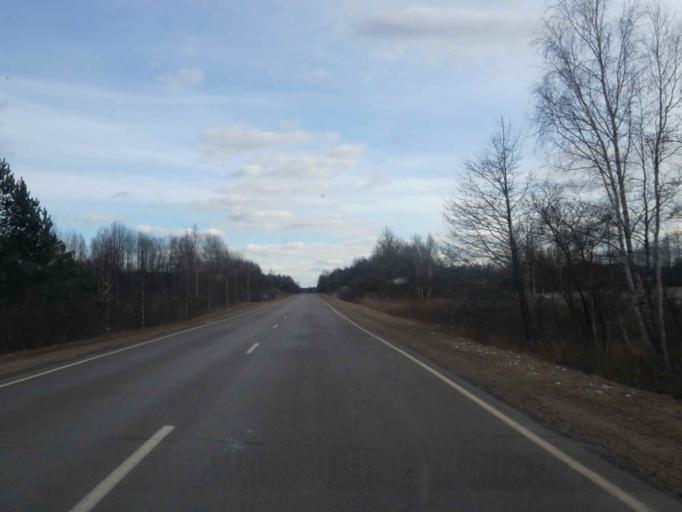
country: BY
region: Minsk
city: Myadzyel
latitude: 54.9484
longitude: 26.9053
